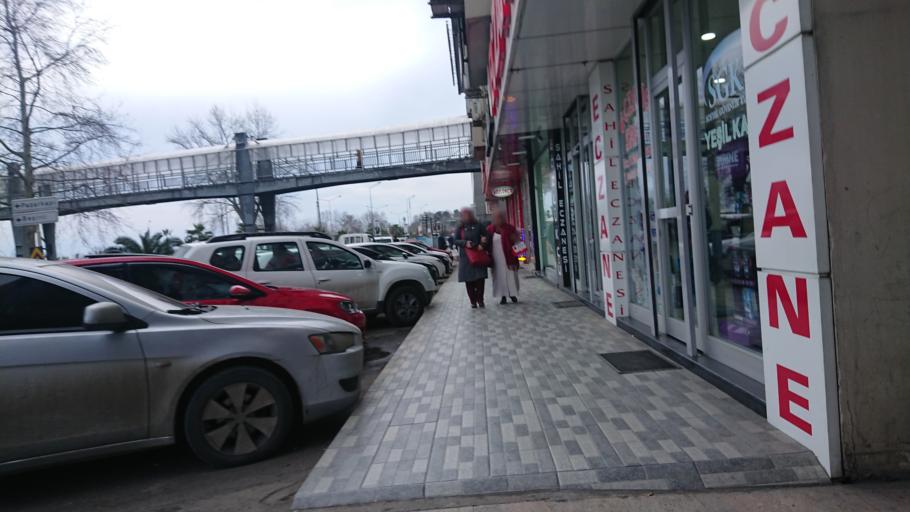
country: TR
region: Trabzon
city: Trabzon
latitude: 41.0085
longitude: 39.7267
